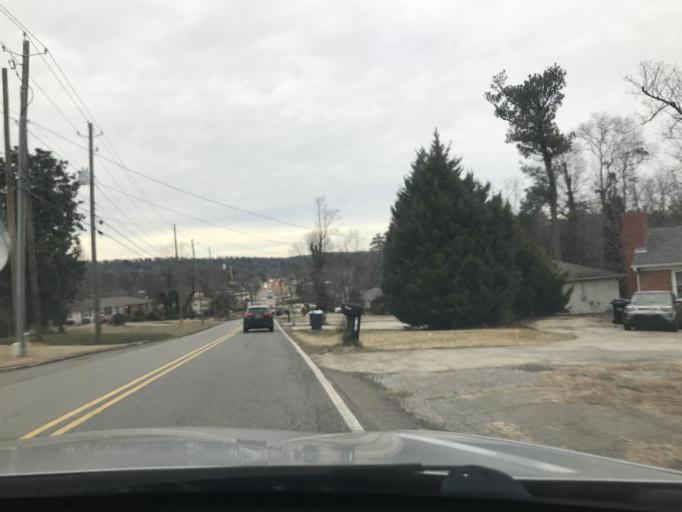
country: US
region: Alabama
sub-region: Jefferson County
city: Cahaba Heights
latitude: 33.4570
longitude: -86.7310
